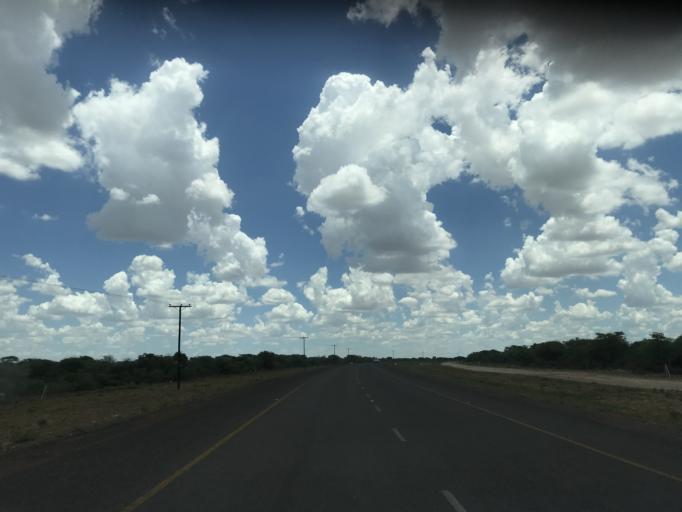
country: BW
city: Mabuli
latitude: -25.8074
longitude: 24.7513
